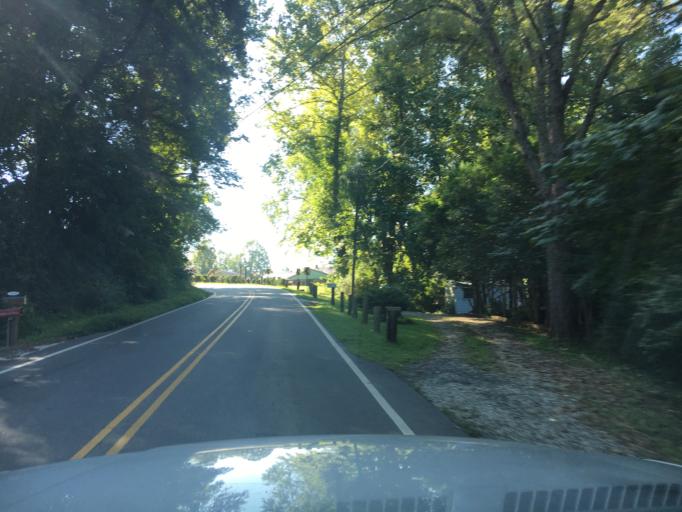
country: US
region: North Carolina
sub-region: McDowell County
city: West Marion
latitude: 35.6688
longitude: -82.0290
